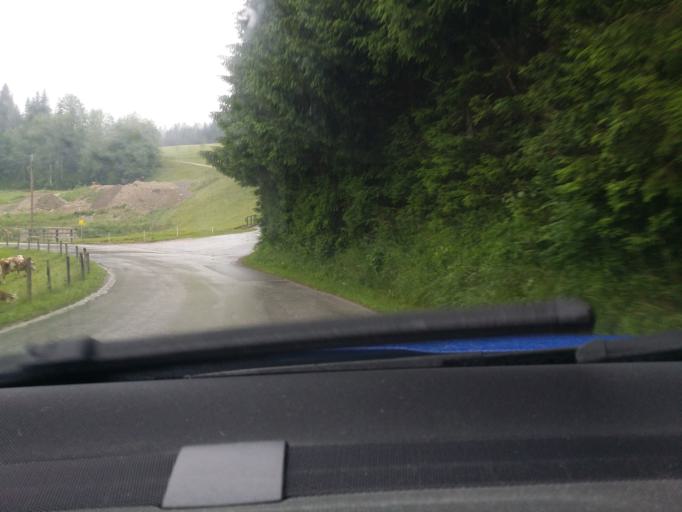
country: AT
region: Salzburg
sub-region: Politischer Bezirk Hallein
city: Abtenau
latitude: 47.5885
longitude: 13.3430
